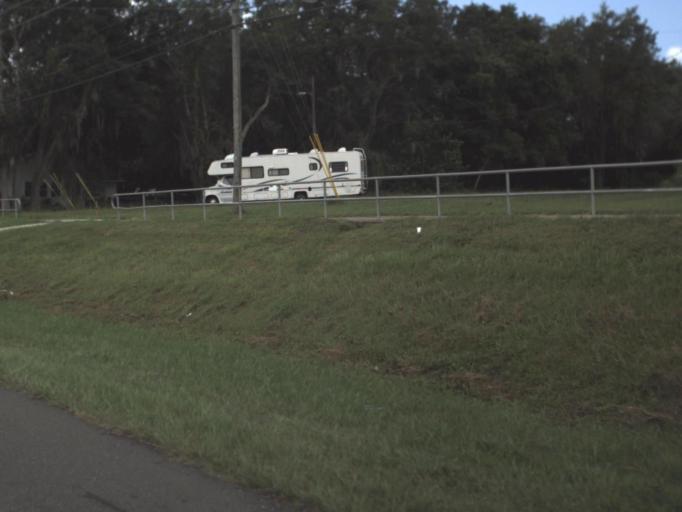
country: US
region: Florida
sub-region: Pinellas County
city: Safety Harbor
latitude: 28.0009
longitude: -82.7090
